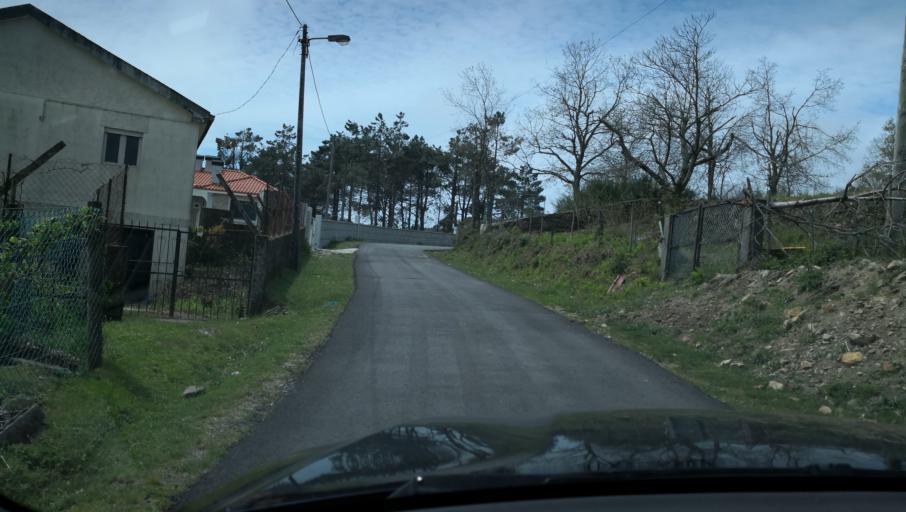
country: PT
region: Vila Real
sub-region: Vila Real
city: Vila Real
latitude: 41.2922
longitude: -7.8185
